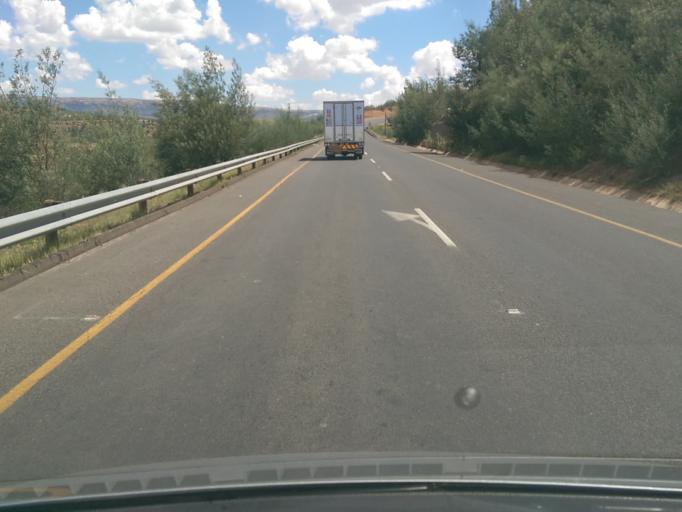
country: LS
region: Maseru
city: Maseru
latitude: -29.3990
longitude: 27.5336
